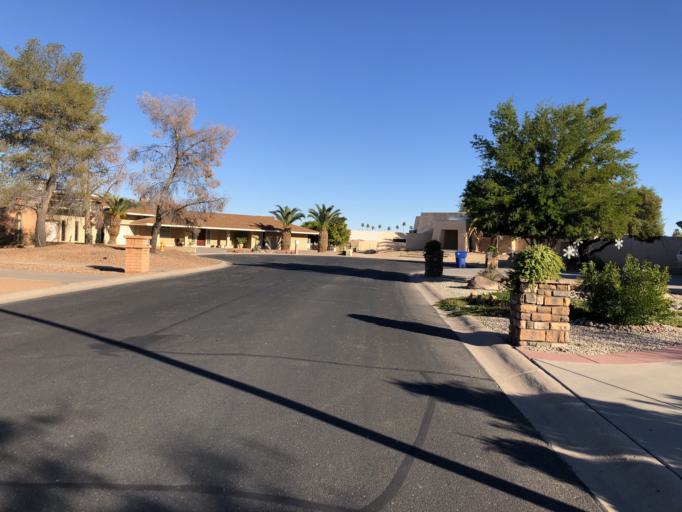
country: US
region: Arizona
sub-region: Maricopa County
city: Chandler
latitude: 33.3010
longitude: -111.9174
